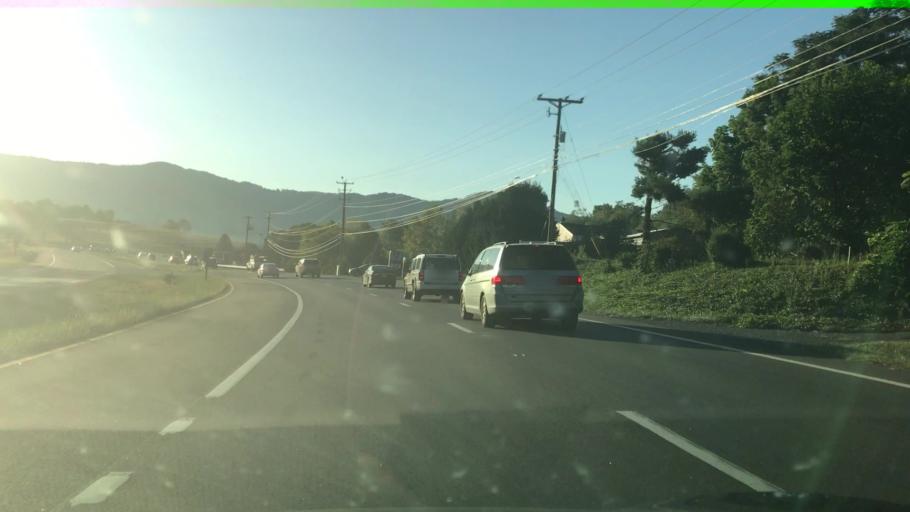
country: US
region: Virginia
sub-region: Botetourt County
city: Laymantown
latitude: 37.3437
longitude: -79.8808
